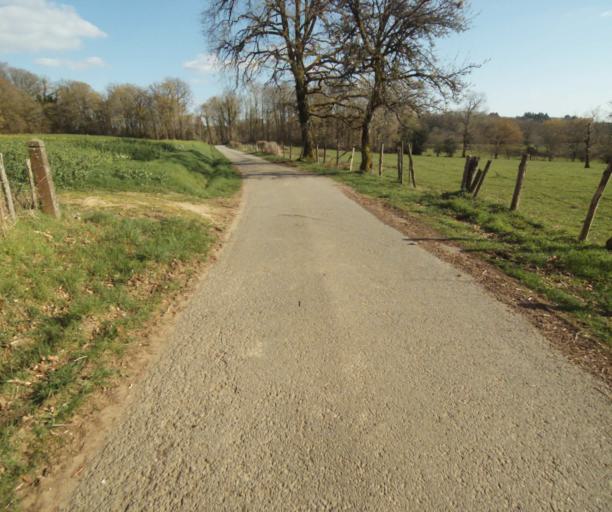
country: FR
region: Limousin
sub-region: Departement de la Correze
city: Saint-Mexant
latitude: 45.3411
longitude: 1.6041
